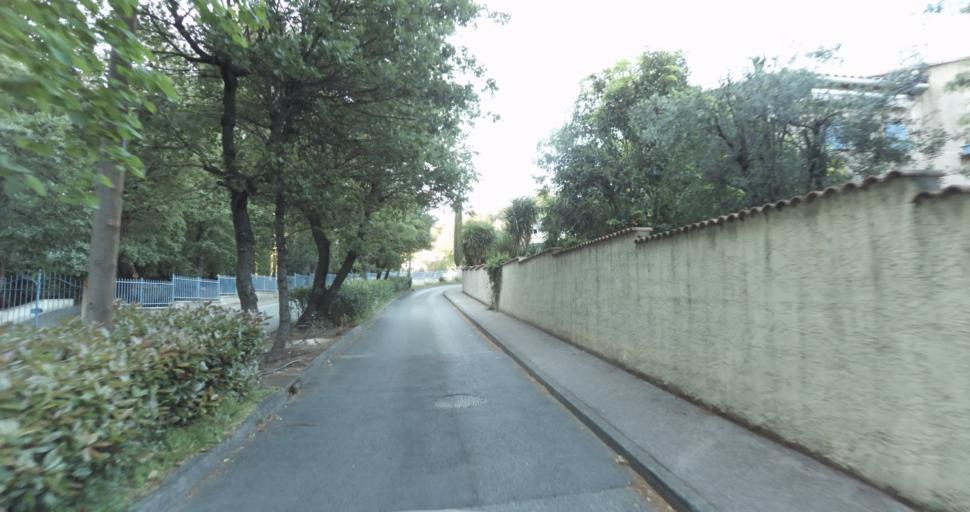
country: FR
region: Provence-Alpes-Cote d'Azur
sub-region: Departement du Var
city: Le Revest-les-Eaux
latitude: 43.1662
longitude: 5.9371
